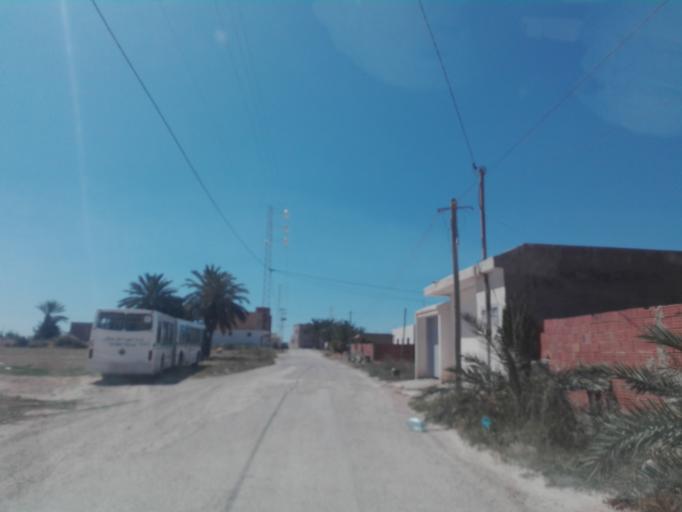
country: TN
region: Safaqis
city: Jabinyanah
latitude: 34.7410
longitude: 11.2985
